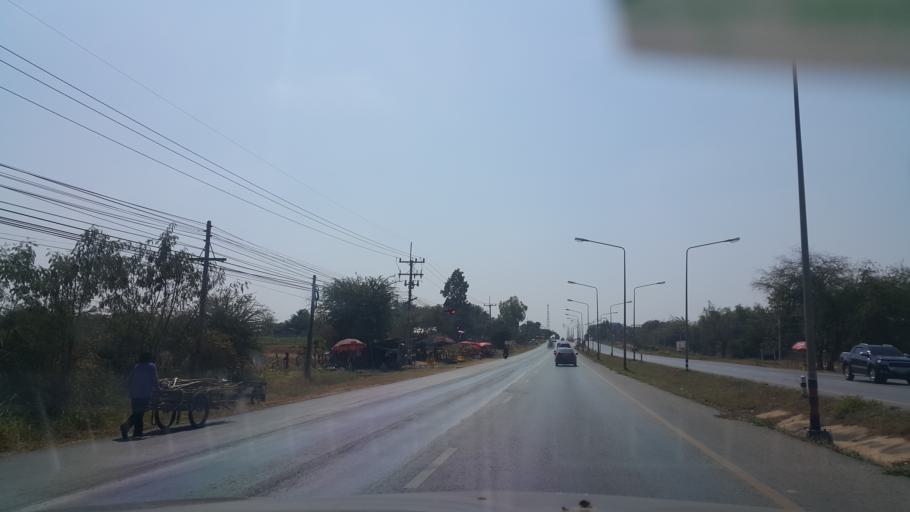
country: TH
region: Khon Kaen
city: Non Sila
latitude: 15.9499
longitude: 102.6827
